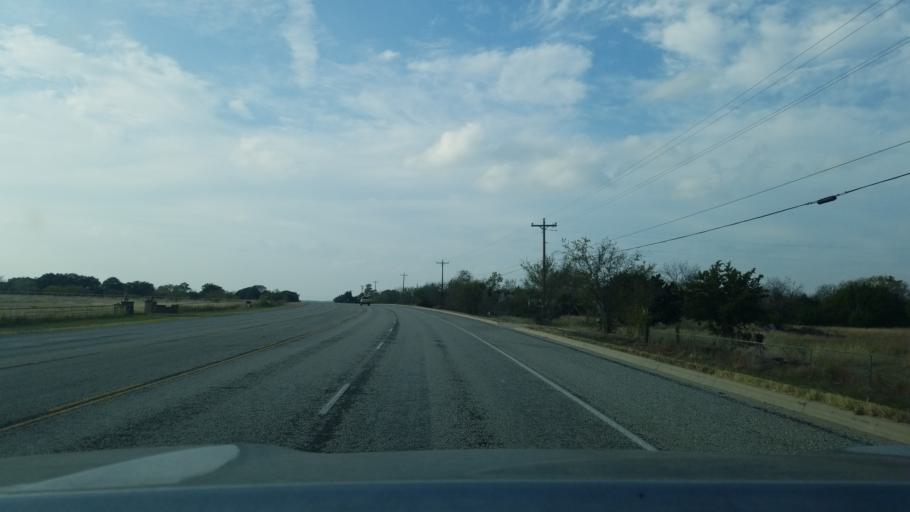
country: US
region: Texas
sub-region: Lampasas County
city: Lampasas
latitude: 31.2222
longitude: -98.3978
